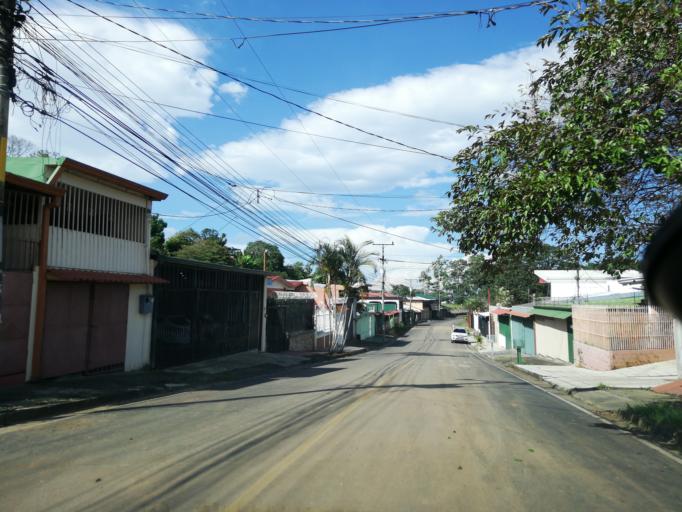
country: CR
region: Alajuela
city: Alajuela
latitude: 10.0091
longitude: -84.2054
